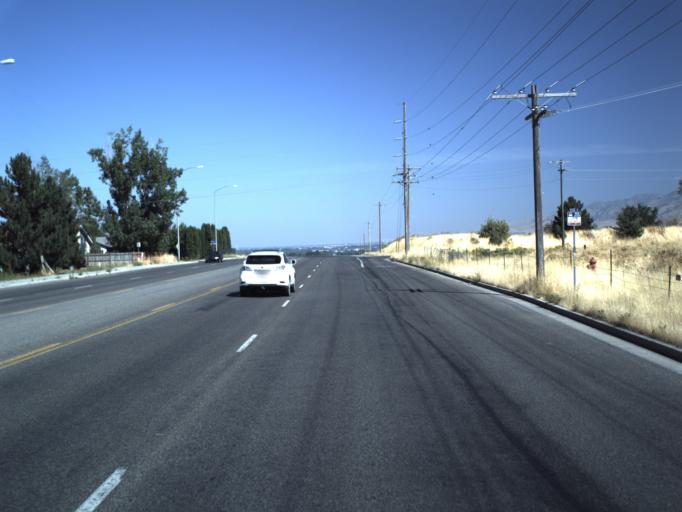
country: US
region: Utah
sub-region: Cache County
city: Hyrum
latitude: 41.6407
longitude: -111.8326
